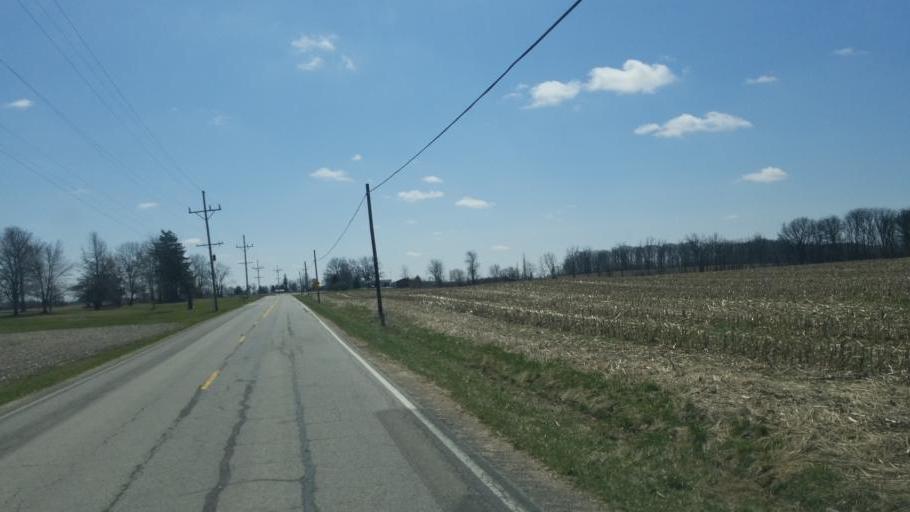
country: US
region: Ohio
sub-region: Marion County
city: Marion
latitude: 40.6398
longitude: -83.2179
